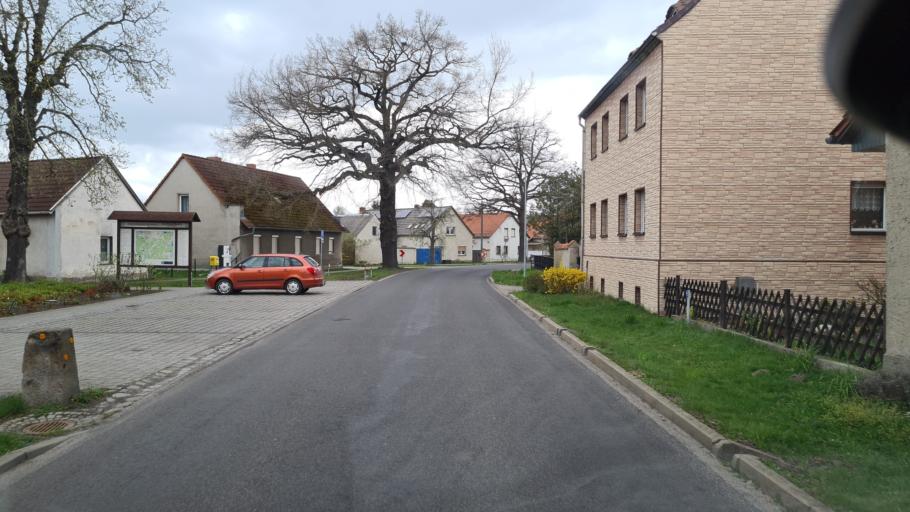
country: DE
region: Brandenburg
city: Schwarzbach
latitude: 51.4521
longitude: 13.9354
